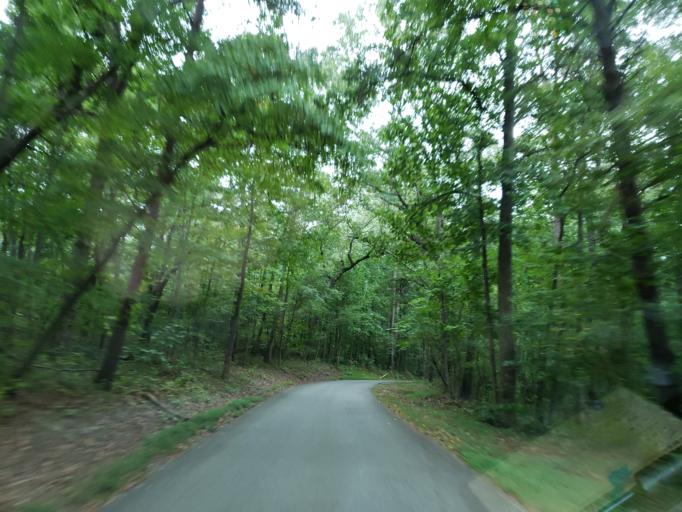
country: US
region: Georgia
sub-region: Cherokee County
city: Ball Ground
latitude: 34.3528
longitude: -84.4851
